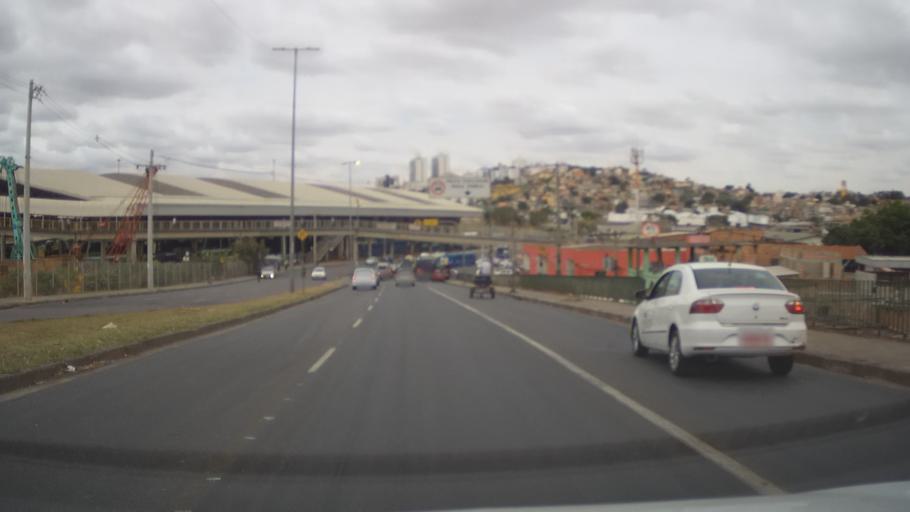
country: BR
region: Minas Gerais
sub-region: Belo Horizonte
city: Belo Horizonte
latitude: -19.8620
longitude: -43.9267
